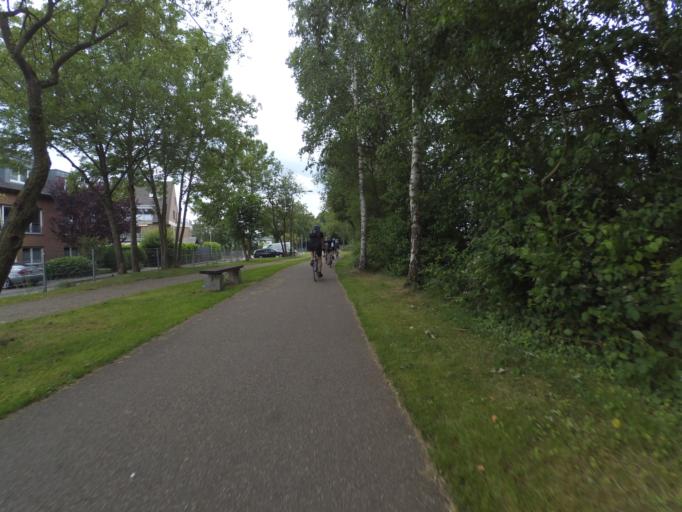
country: DE
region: North Rhine-Westphalia
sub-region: Regierungsbezirk Koln
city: Wurselen
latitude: 50.7554
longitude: 6.1580
